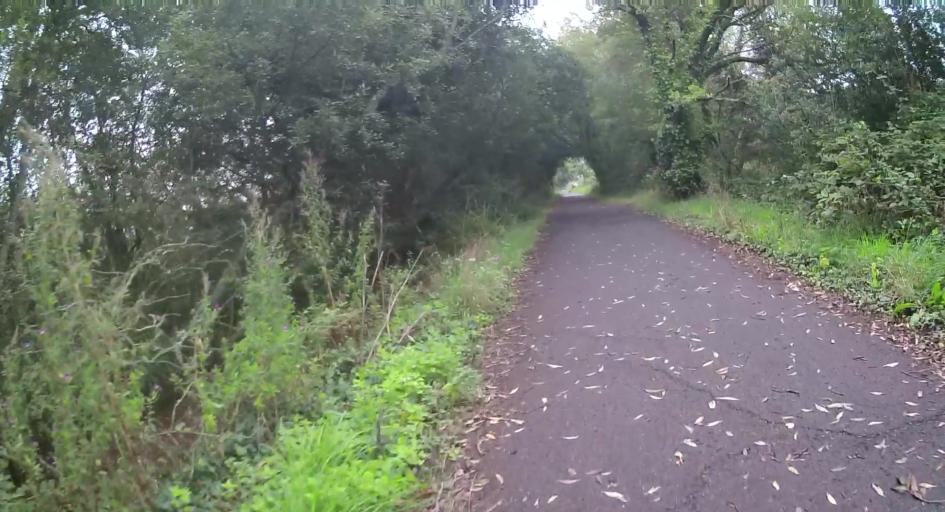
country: GB
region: England
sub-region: Isle of Wight
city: Newchurch
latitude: 50.6706
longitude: -1.1985
